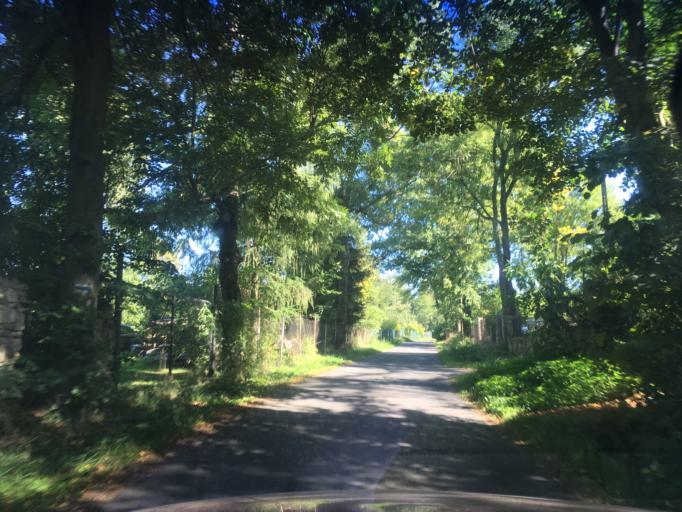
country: PL
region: Lower Silesian Voivodeship
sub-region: Powiat lubanski
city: Swieradow-Zdroj
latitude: 50.9495
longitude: 15.3195
